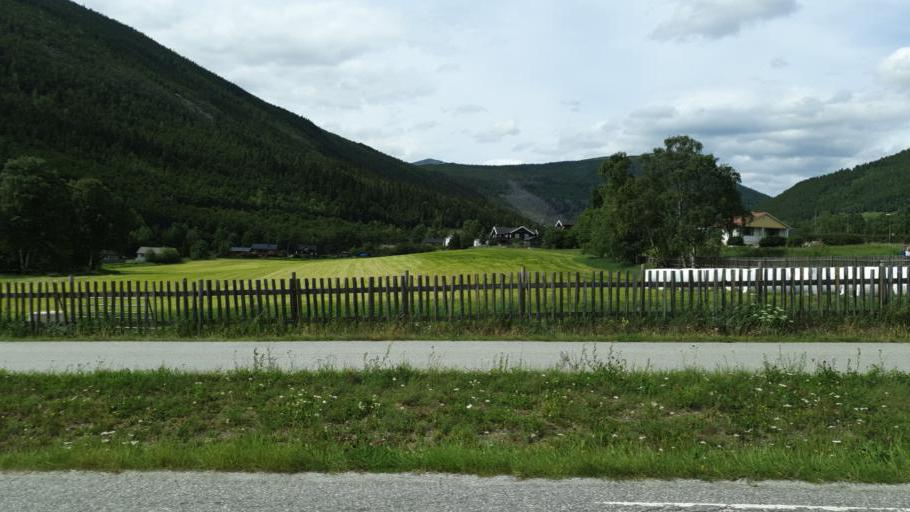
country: NO
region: Oppland
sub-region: Sel
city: Otta
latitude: 61.8483
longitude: 9.4206
